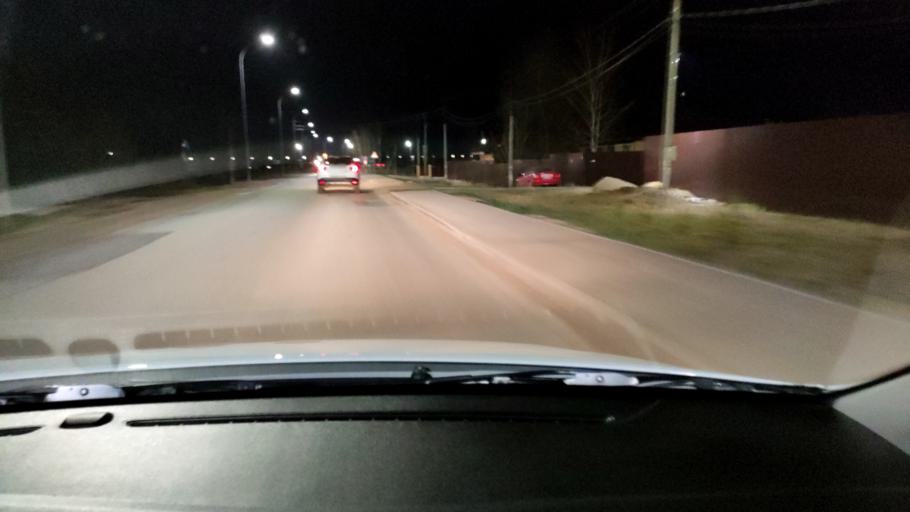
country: RU
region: Tatarstan
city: Stolbishchi
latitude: 55.6937
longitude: 49.2127
